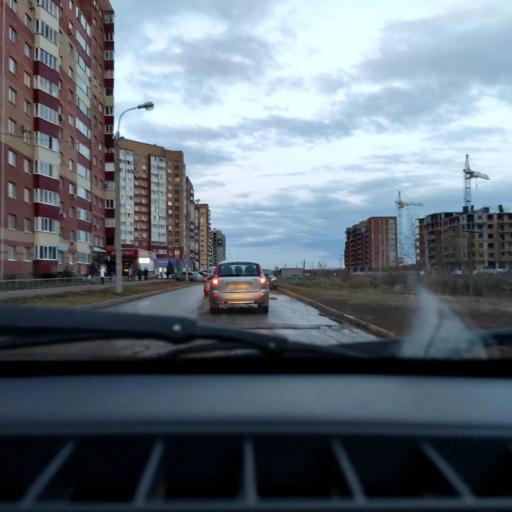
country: RU
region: Bashkortostan
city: Mikhaylovka
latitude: 54.7121
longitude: 55.8406
